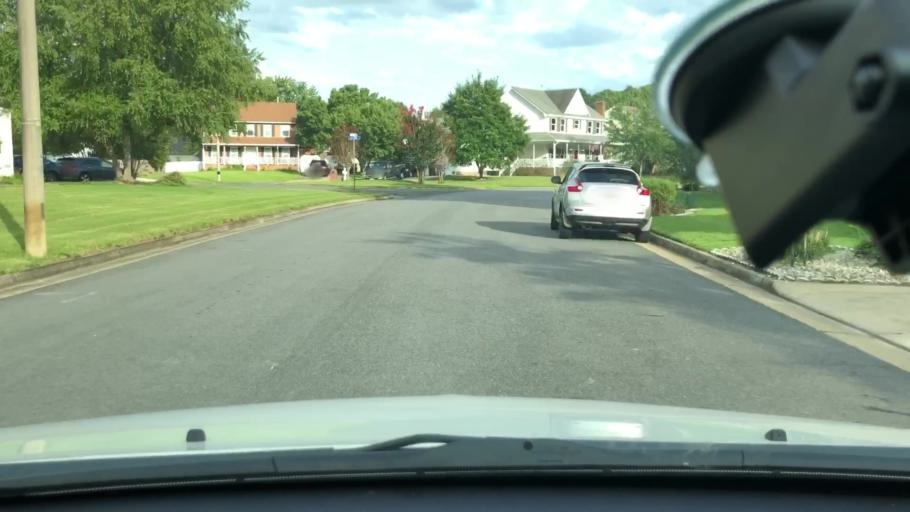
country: US
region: Virginia
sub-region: City of Chesapeake
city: Chesapeake
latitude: 36.7178
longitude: -76.2736
